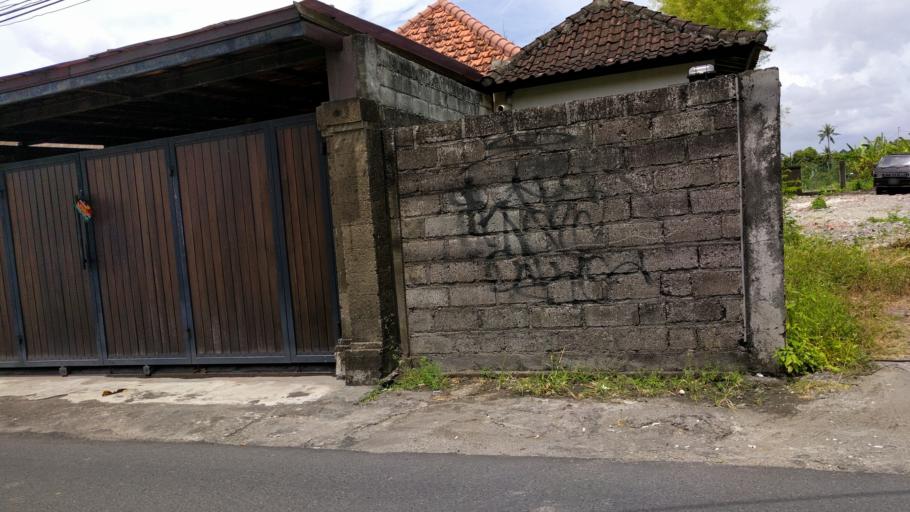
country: ID
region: Bali
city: Banjar Gunungpande
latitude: -8.6679
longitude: 115.1473
